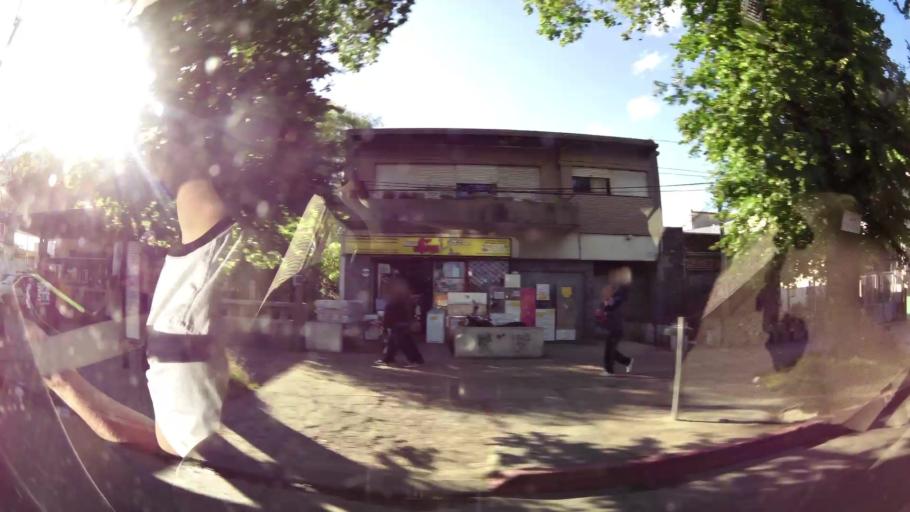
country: UY
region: Montevideo
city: Montevideo
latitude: -34.8647
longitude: -56.2344
